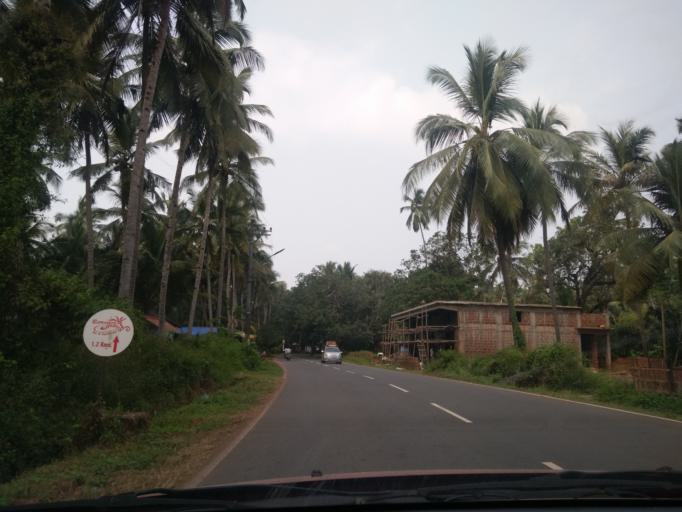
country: IN
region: Goa
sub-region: North Goa
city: Goa Velha
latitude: 15.4360
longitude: 73.8941
